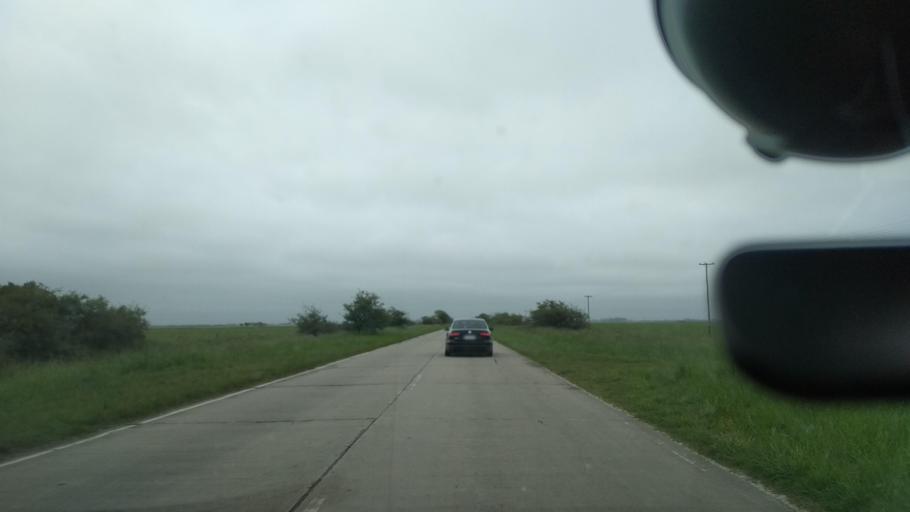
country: AR
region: Buenos Aires
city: Veronica
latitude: -35.5746
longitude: -57.2823
